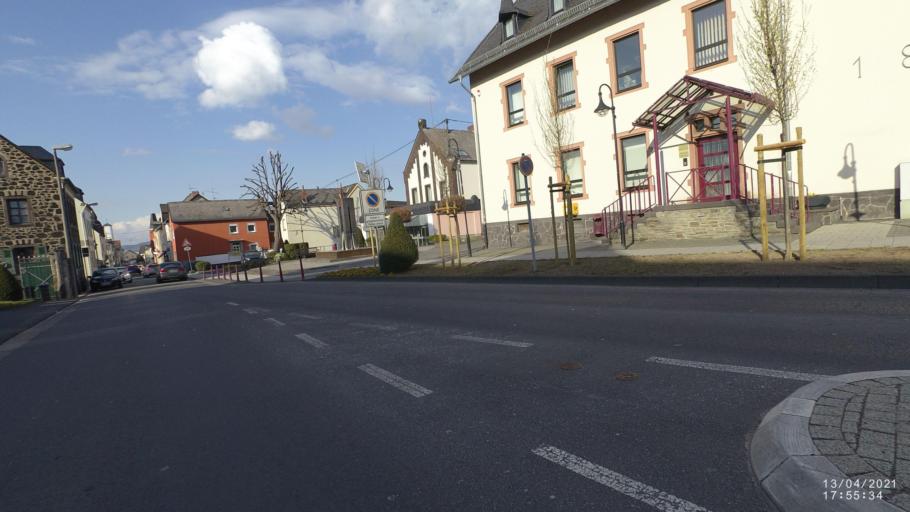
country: DE
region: Rheinland-Pfalz
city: Mulheim-Karlich
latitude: 50.3871
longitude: 7.4974
